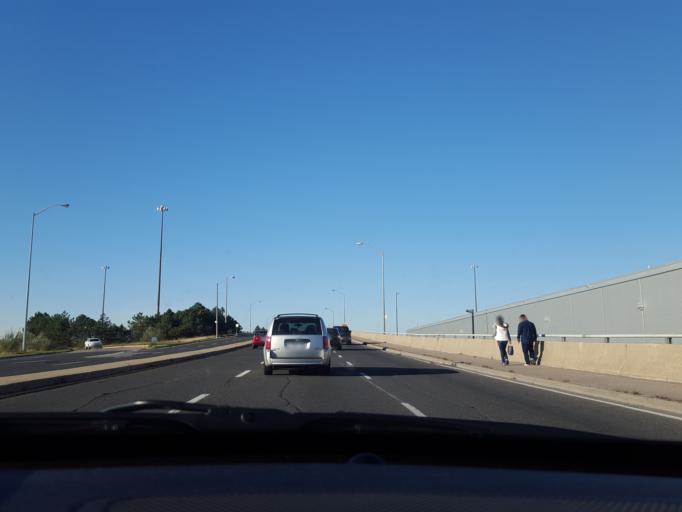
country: CA
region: Ontario
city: Scarborough
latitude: 43.7770
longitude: -79.2637
